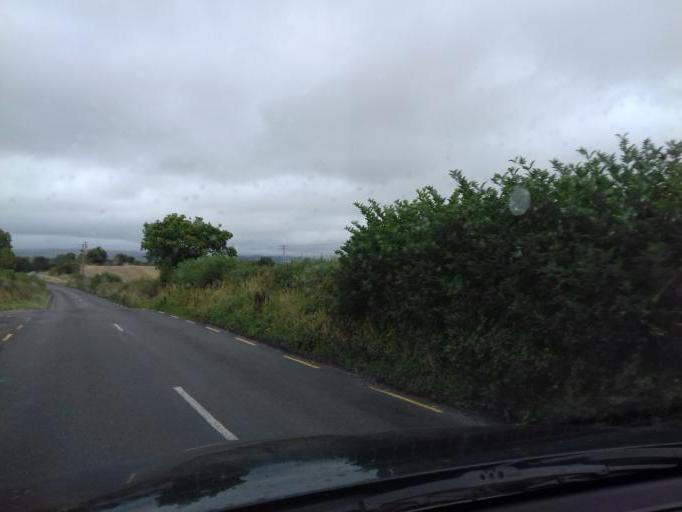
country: IE
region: Leinster
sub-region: County Carlow
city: Bagenalstown
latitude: 52.7206
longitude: -6.9664
